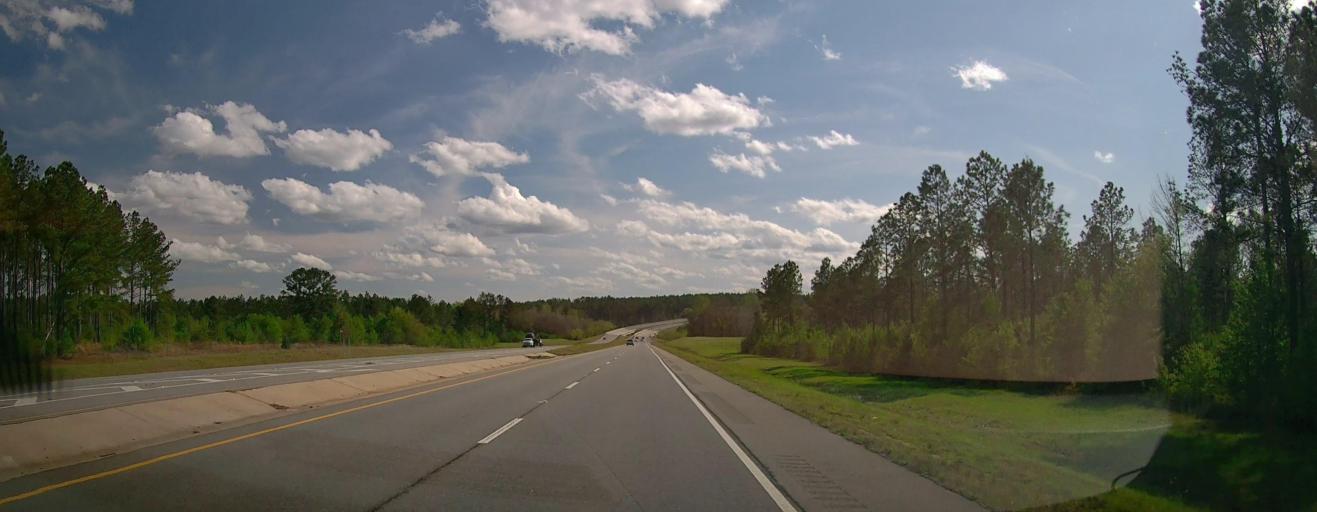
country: US
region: Georgia
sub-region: Baldwin County
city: Hardwick
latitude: 32.9898
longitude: -83.2053
